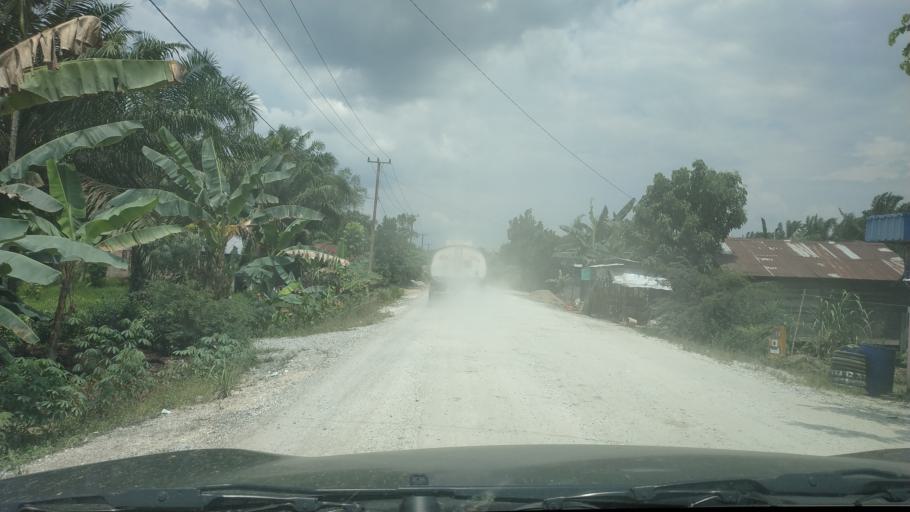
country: ID
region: Riau
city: Sungaisalak
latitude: -0.5996
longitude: 102.9015
